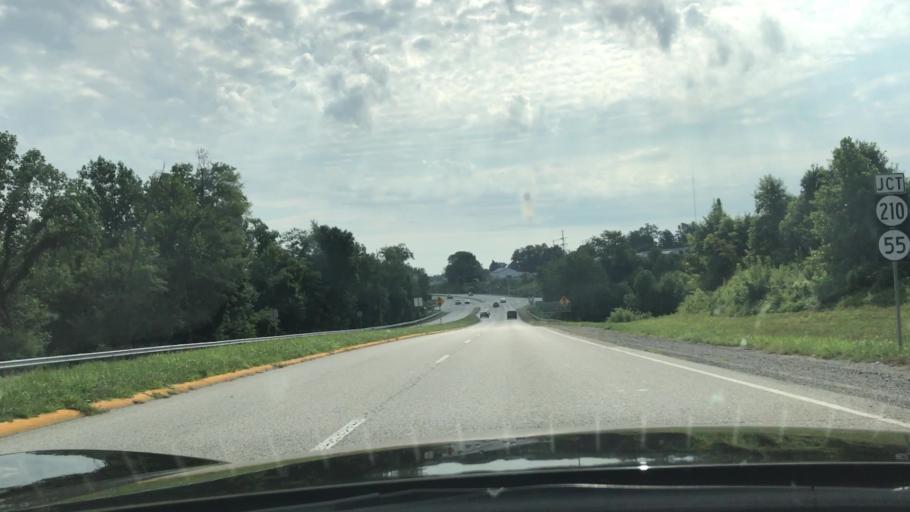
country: US
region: Kentucky
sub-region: Taylor County
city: Campbellsville
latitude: 37.3380
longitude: -85.3640
